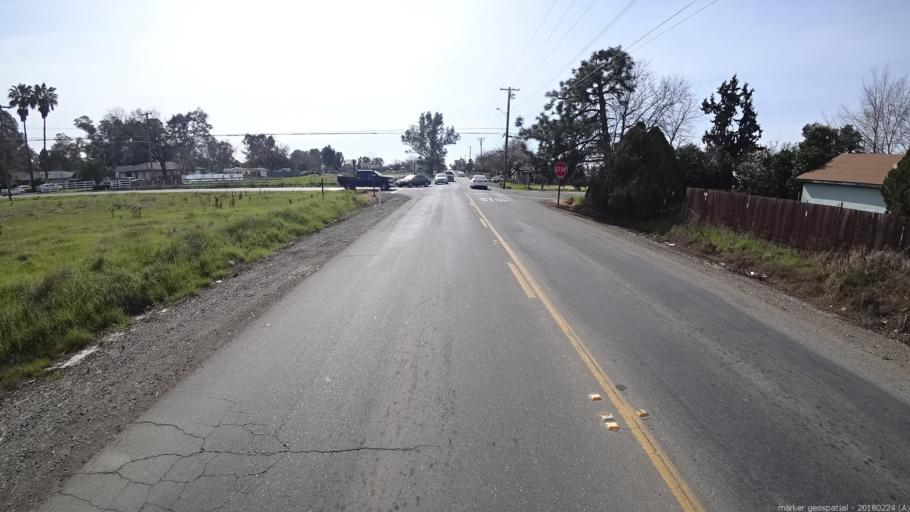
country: US
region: California
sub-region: Sacramento County
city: Rio Linda
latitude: 38.6767
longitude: -121.4291
